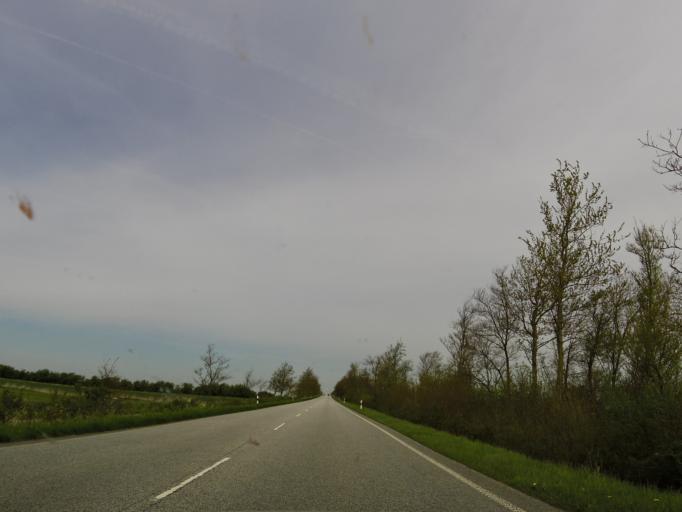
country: DE
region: Schleswig-Holstein
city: Lohe-Rickelshof
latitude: 54.2151
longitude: 9.0457
